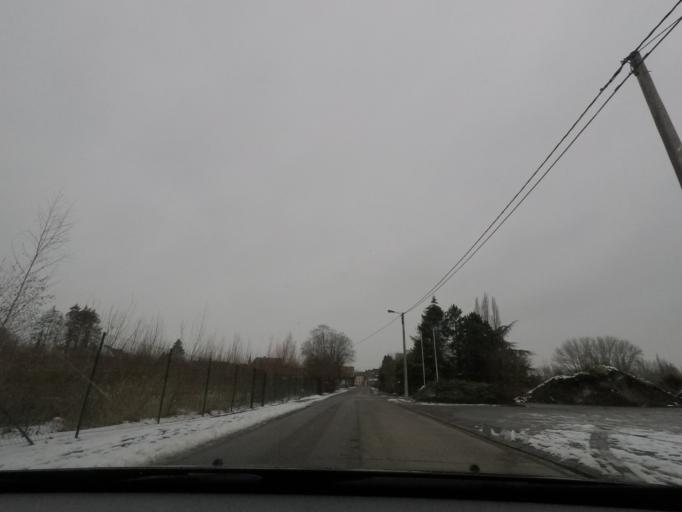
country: BE
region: Wallonia
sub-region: Province du Hainaut
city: Brugelette
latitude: 50.5943
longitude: 3.8560
